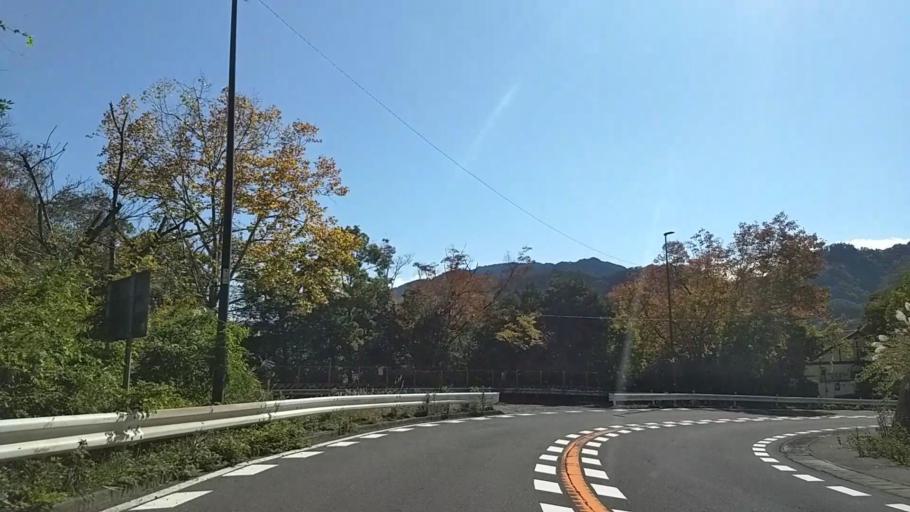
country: JP
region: Yamanashi
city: Uenohara
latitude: 35.6197
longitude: 139.1717
